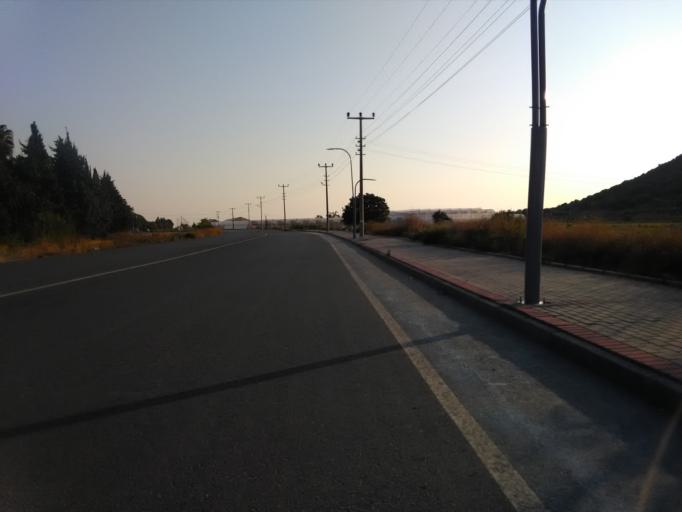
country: TR
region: Antalya
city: Gazipasa
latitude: 36.2589
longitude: 32.2905
